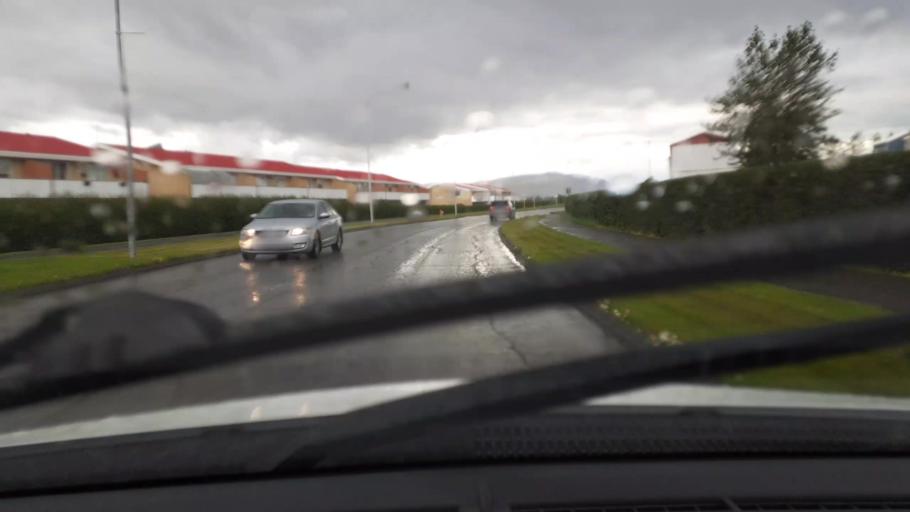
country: IS
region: West
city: Akranes
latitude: 64.3211
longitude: -22.0551
